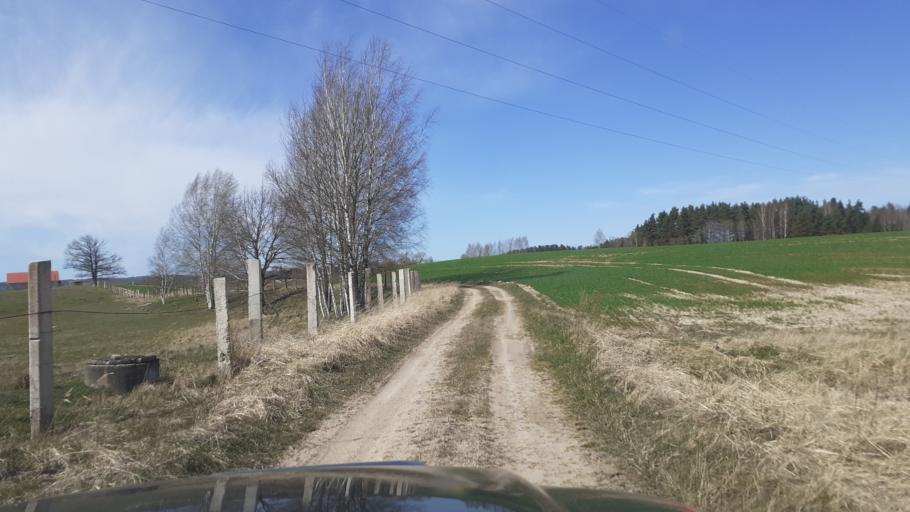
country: LV
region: Skrunda
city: Skrunda
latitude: 56.8302
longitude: 22.0137
